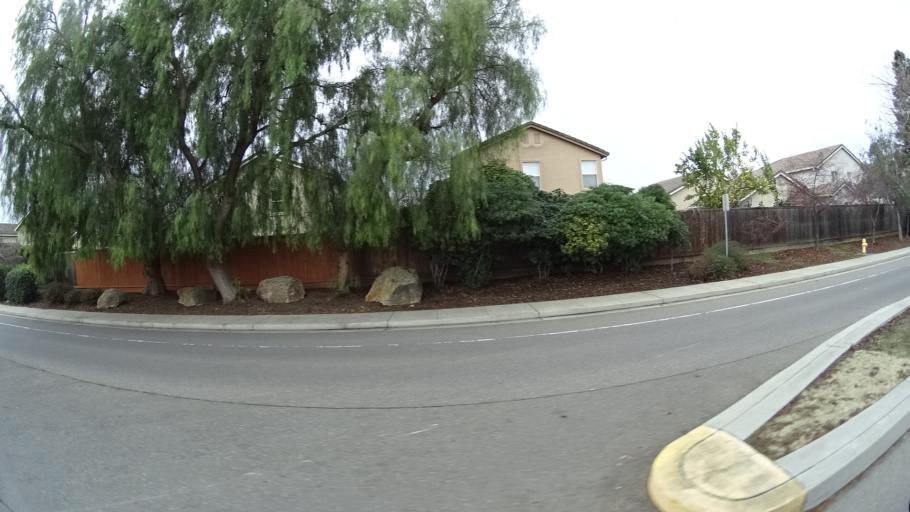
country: US
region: California
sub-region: Yolo County
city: Davis
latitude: 38.5660
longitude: -121.7241
